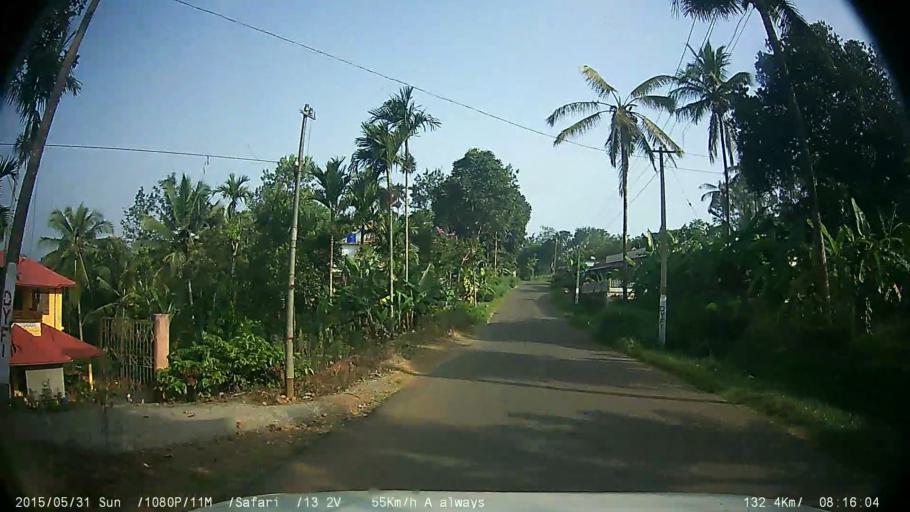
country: IN
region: Kerala
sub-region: Wayanad
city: Kalpetta
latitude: 11.6534
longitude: 75.9989
